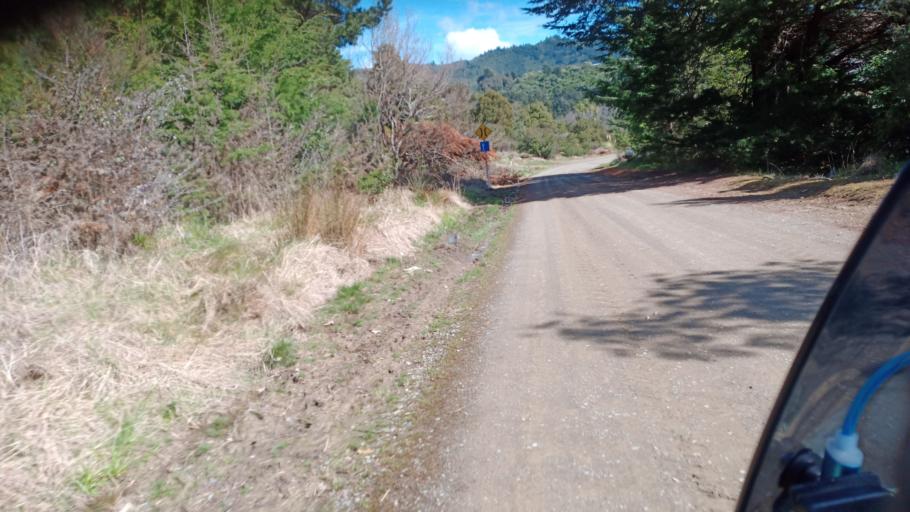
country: NZ
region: Hawke's Bay
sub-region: Wairoa District
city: Wairoa
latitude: -38.8136
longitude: 177.1532
